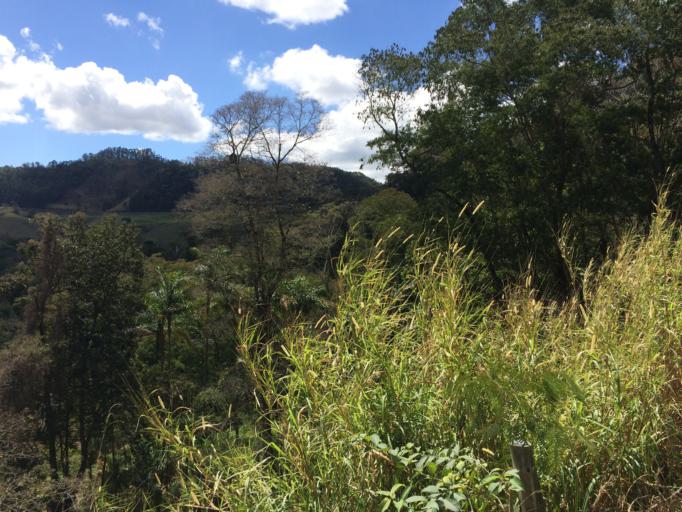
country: BR
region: Espirito Santo
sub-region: Vargem Alta
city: Vargem Alta
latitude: -20.6889
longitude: -41.0336
